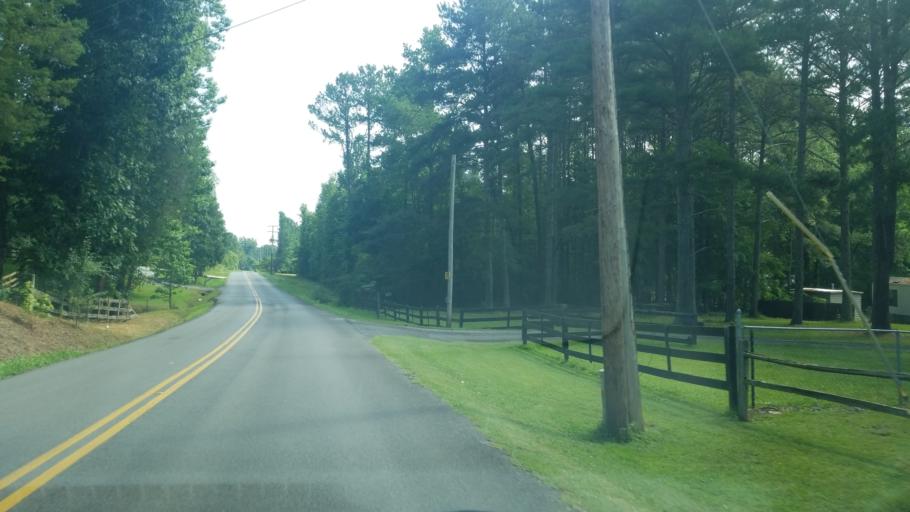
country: US
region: Tennessee
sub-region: Hamilton County
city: Apison
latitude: 35.0832
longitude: -84.9717
